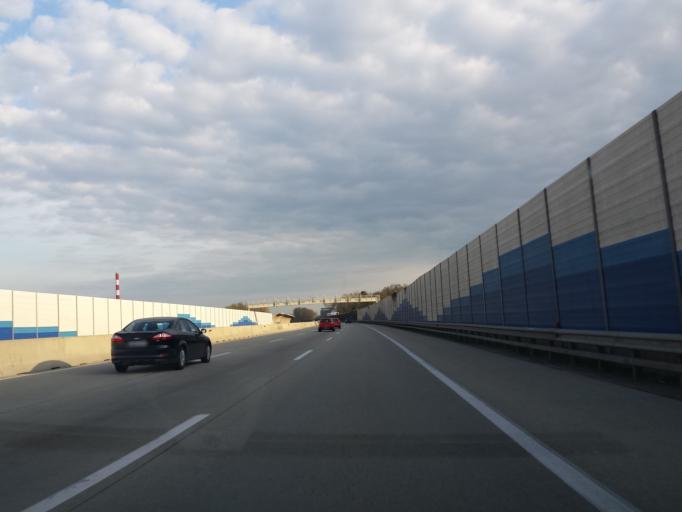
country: AT
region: Lower Austria
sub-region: Politischer Bezirk Korneuburg
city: Korneuburg
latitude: 48.3425
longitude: 16.3225
